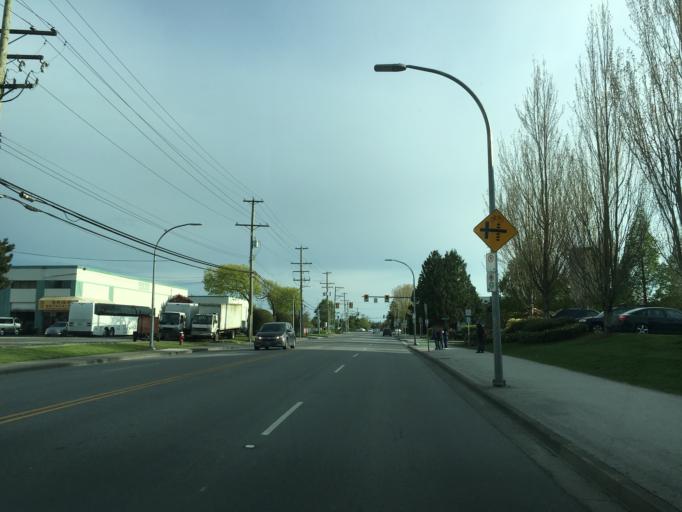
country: CA
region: British Columbia
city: Richmond
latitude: 49.1725
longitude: -123.0692
